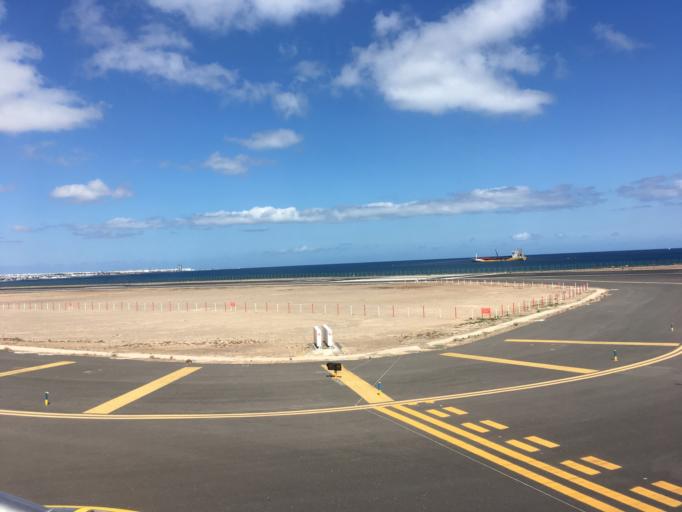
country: ES
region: Canary Islands
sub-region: Provincia de Las Palmas
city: Tias
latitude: 28.9367
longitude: -13.6122
